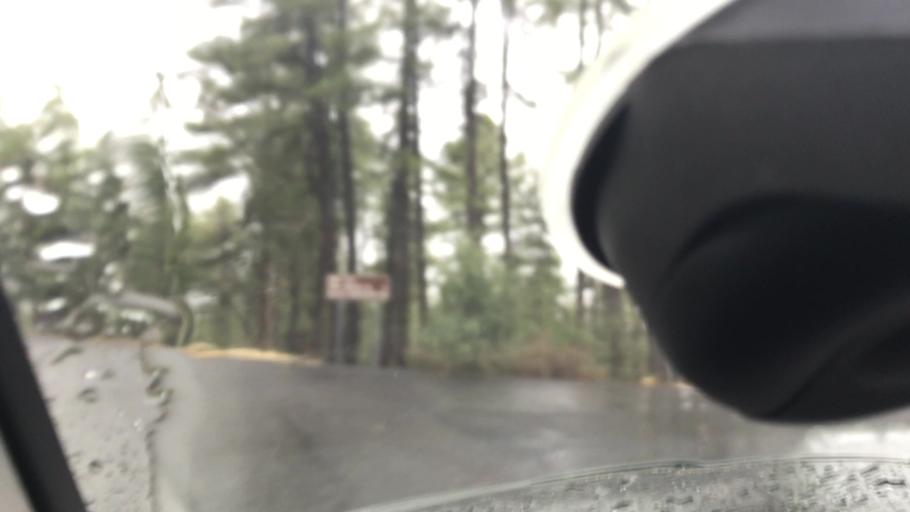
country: US
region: Arizona
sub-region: Yavapai County
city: Prescott
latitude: 34.5076
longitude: -112.3845
